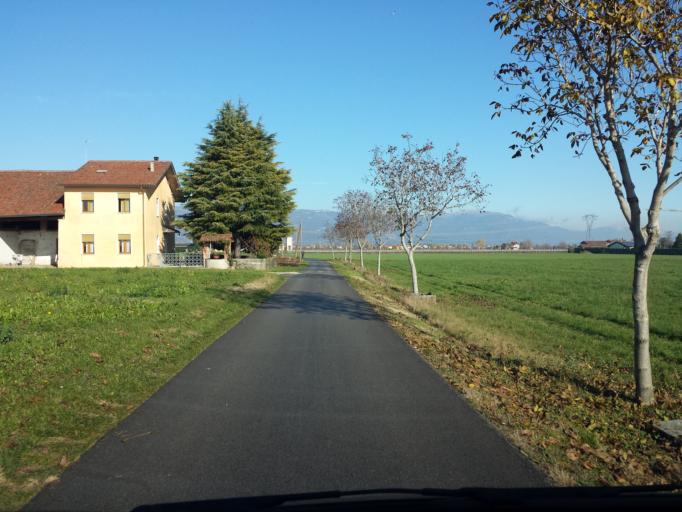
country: IT
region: Veneto
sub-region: Provincia di Vicenza
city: Sandrigo
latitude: 45.6743
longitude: 11.5943
